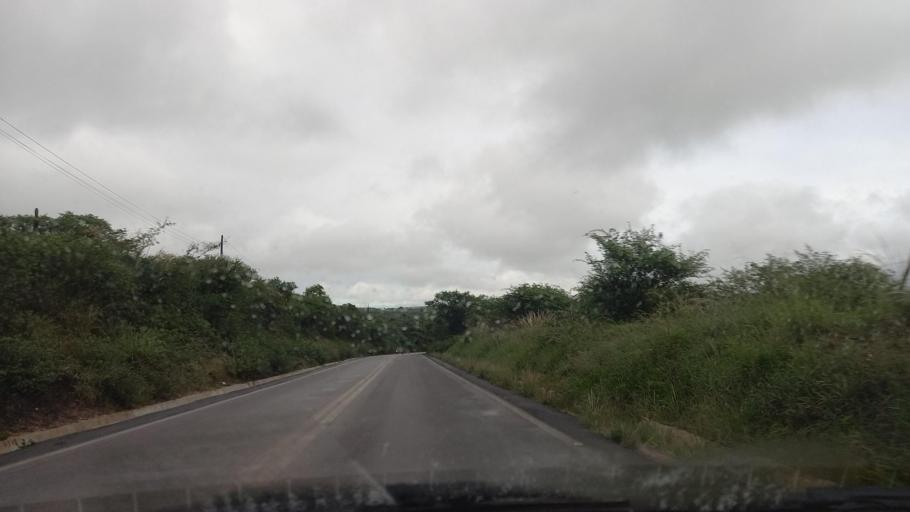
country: BR
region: Pernambuco
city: Garanhuns
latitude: -8.8488
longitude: -36.5188
